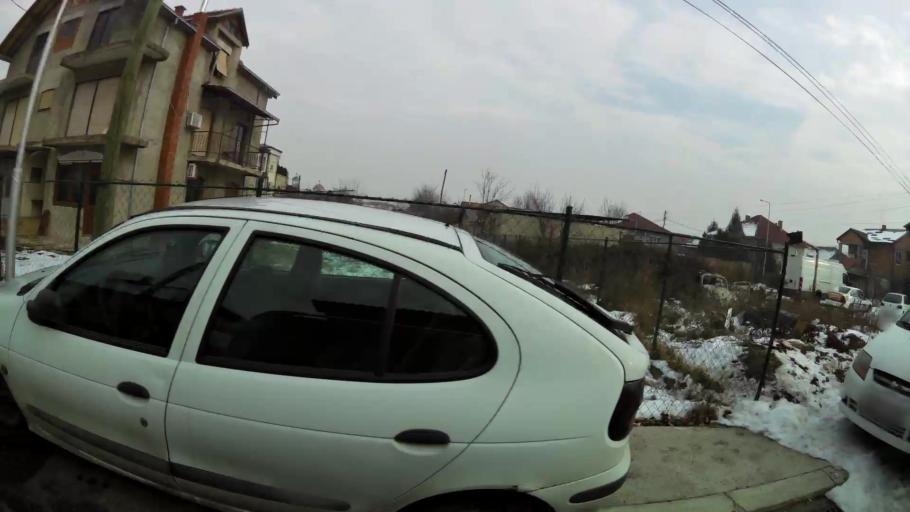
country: MK
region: Saraj
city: Saraj
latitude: 42.0165
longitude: 21.3538
